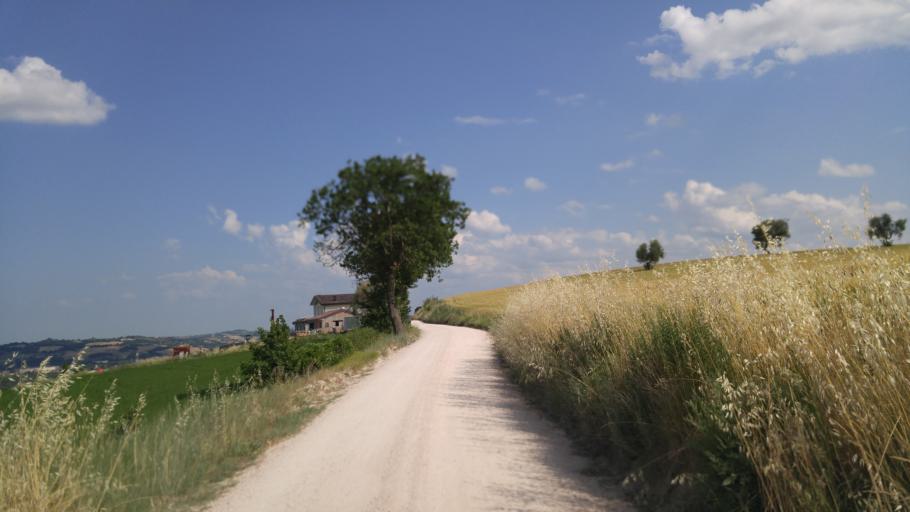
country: IT
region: The Marches
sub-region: Provincia di Pesaro e Urbino
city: Montefelcino
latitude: 43.7276
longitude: 12.8515
